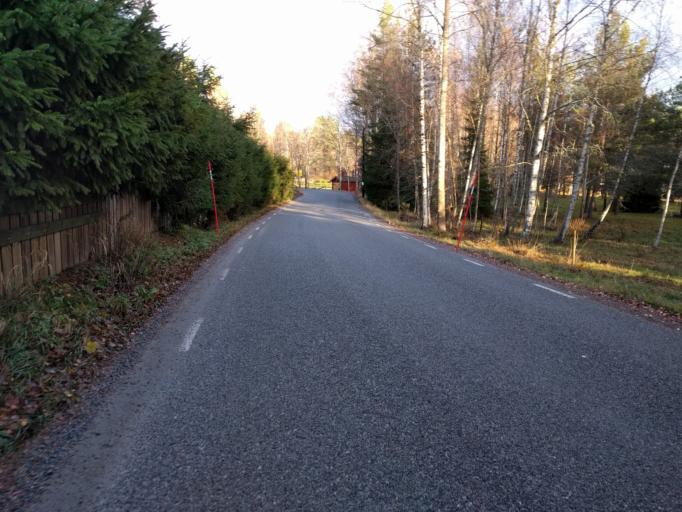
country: SE
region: Stockholm
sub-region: Osterakers Kommun
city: Akersberga
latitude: 59.5960
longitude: 18.3495
